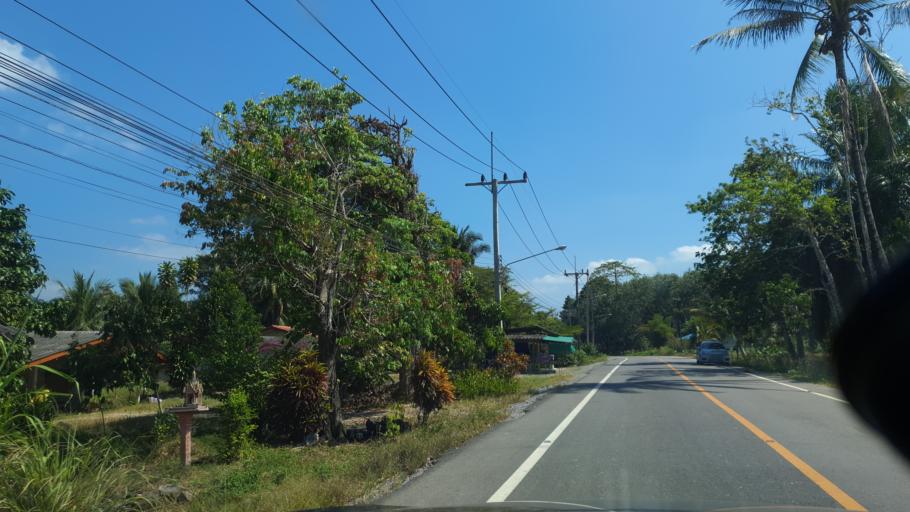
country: TH
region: Krabi
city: Khlong Thom
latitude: 7.9220
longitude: 99.2461
